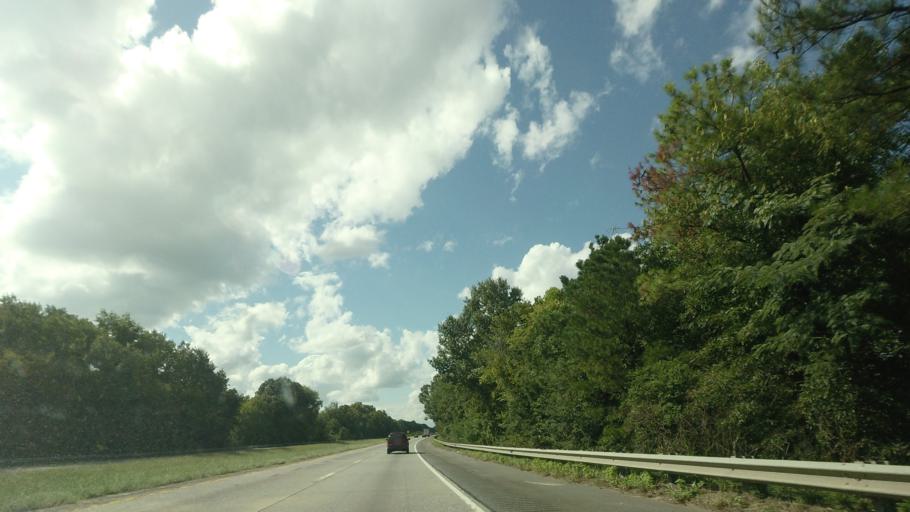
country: US
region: Georgia
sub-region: Bibb County
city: Macon
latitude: 32.8268
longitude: -83.6013
